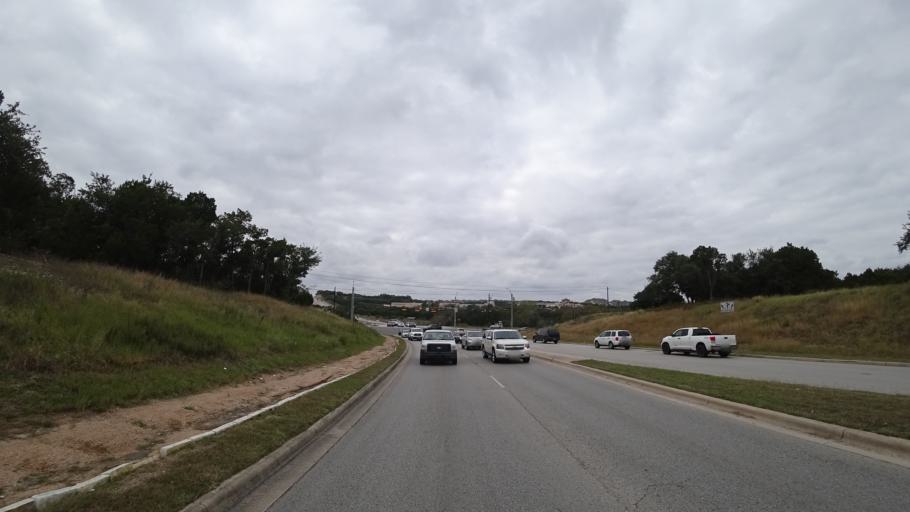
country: US
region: Texas
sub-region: Travis County
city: Bee Cave
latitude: 30.3165
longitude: -97.9487
